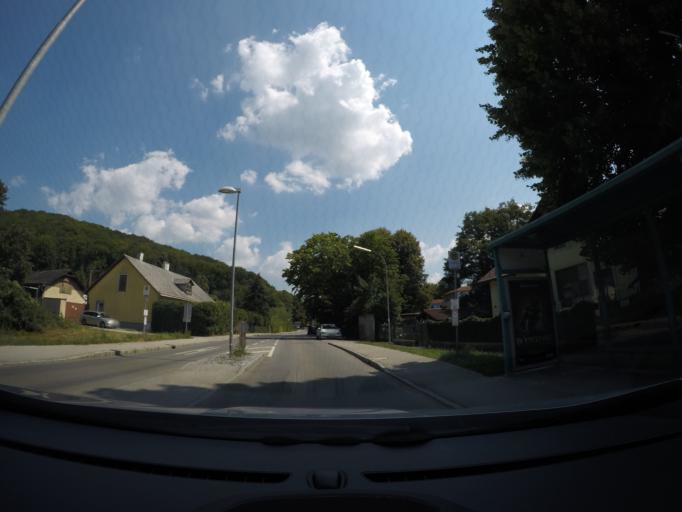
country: AT
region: Lower Austria
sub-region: Politischer Bezirk Wien-Umgebung
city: Purkersdorf
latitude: 48.2315
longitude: 16.1977
